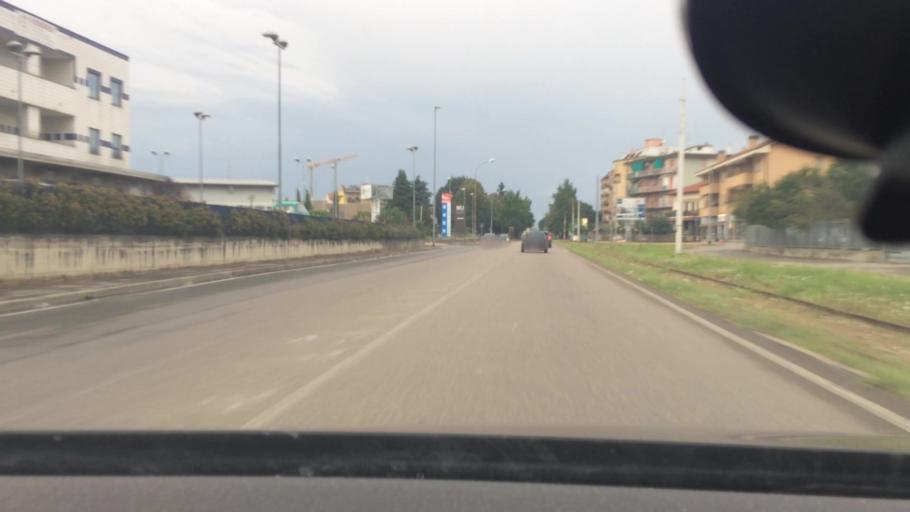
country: IT
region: Lombardy
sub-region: Provincia di Monza e Brianza
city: Nova Milanese
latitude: 45.5796
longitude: 9.1937
